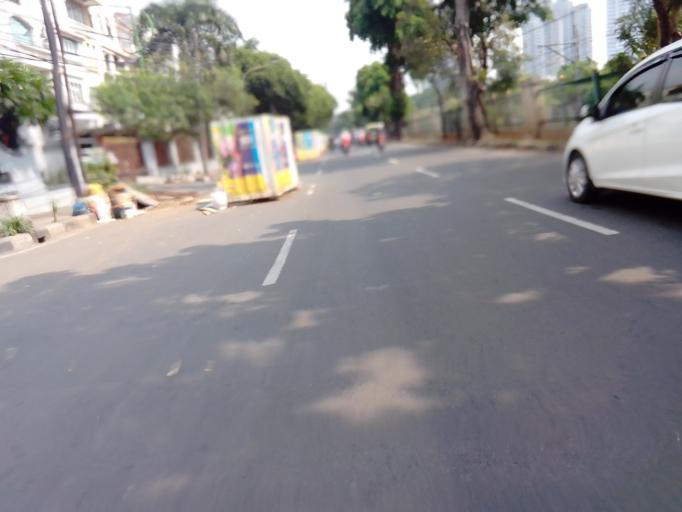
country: ID
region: Jakarta Raya
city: Jakarta
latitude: -6.2206
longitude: 106.7914
